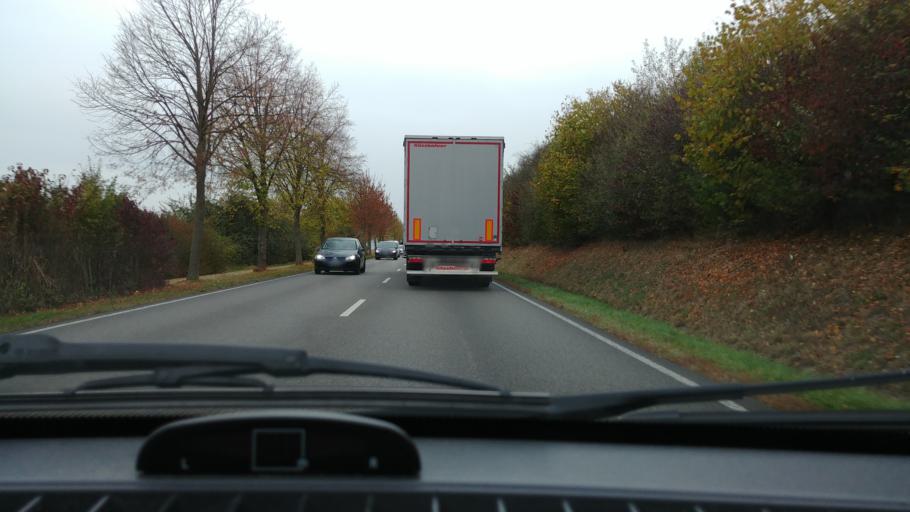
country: DE
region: Baden-Wuerttemberg
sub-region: Regierungsbezirk Stuttgart
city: Bad Mergentheim
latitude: 49.5181
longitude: 9.7496
